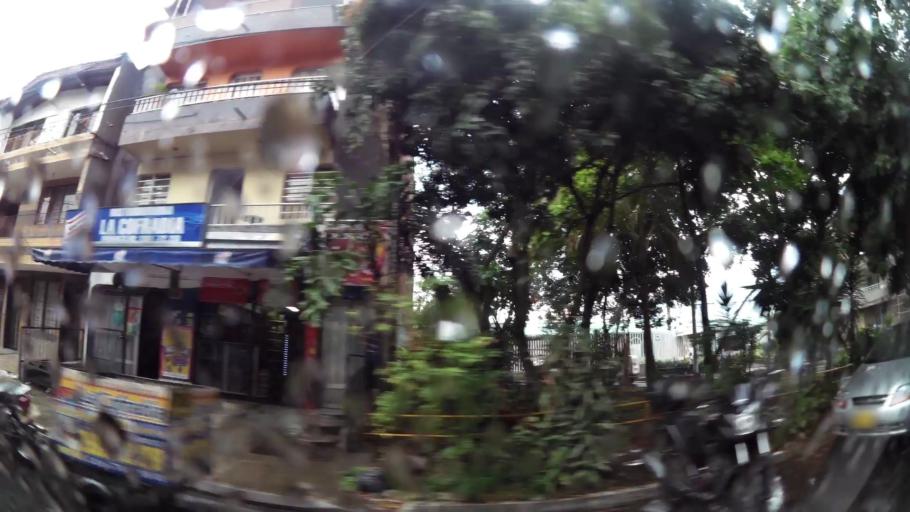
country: CO
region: Antioquia
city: Itagui
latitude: 6.1857
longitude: -75.5943
